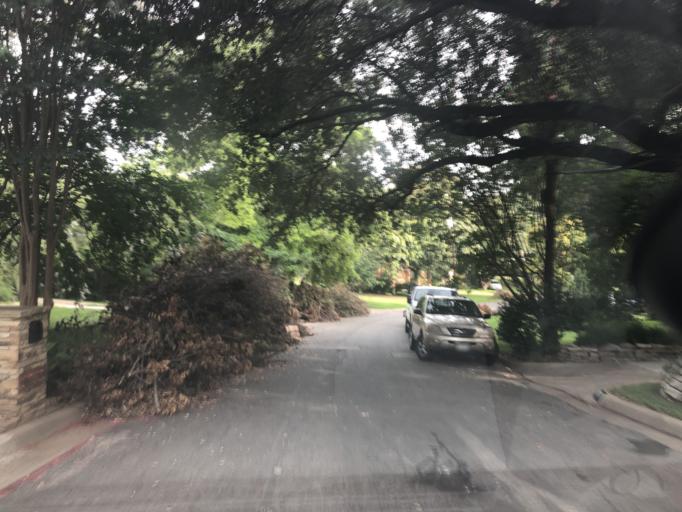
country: US
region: Texas
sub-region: Dallas County
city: University Park
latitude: 32.8572
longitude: -96.8414
